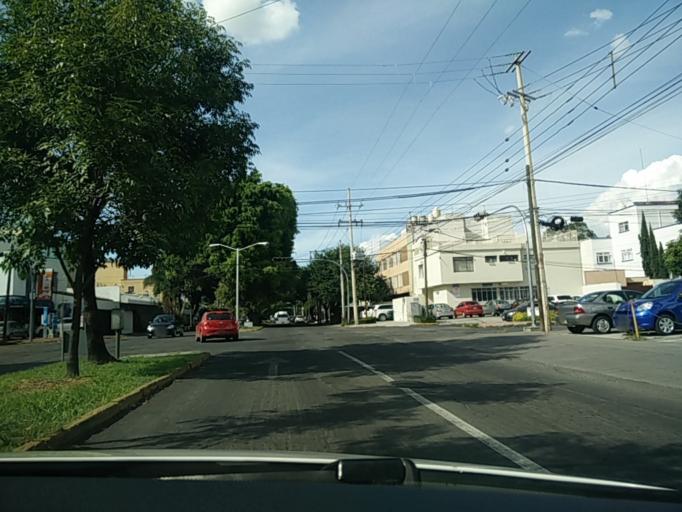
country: MX
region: Jalisco
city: Guadalajara
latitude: 20.6773
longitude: -103.3773
